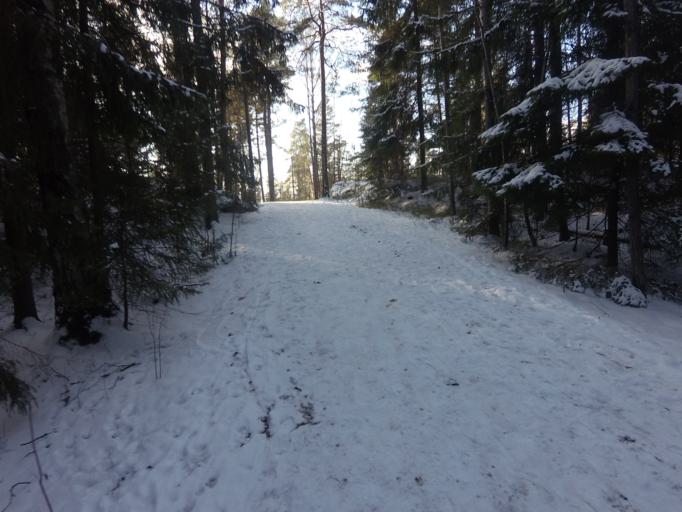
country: FI
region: Uusimaa
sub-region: Helsinki
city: Kauniainen
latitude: 60.1732
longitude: 24.7131
